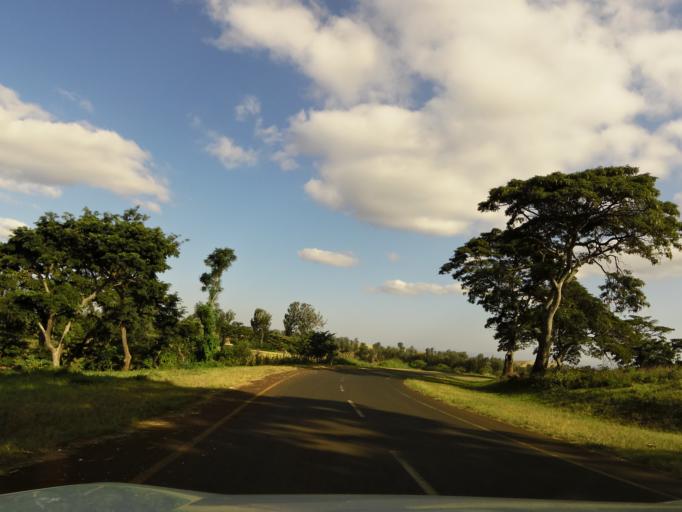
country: TZ
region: Arusha
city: Kiratu
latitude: -3.3115
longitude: 35.5929
